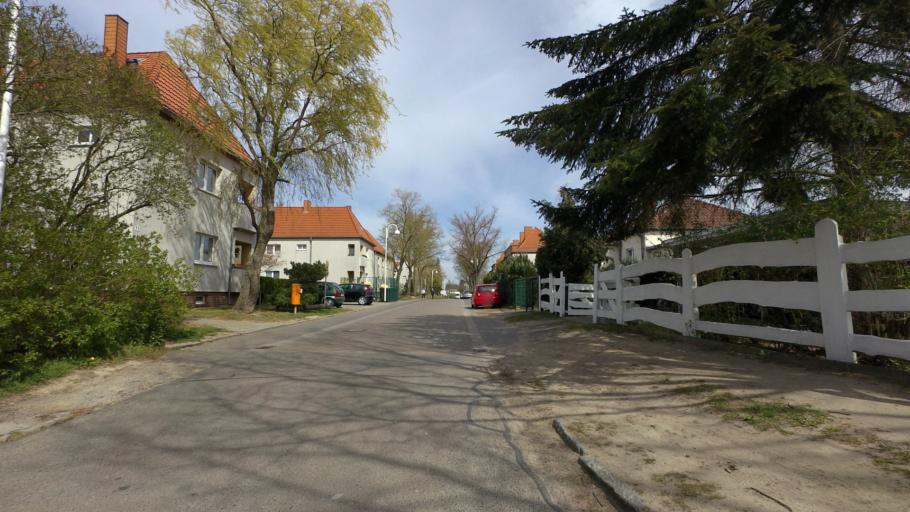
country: DE
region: Berlin
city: Lichtenrade
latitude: 52.3507
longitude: 13.4171
